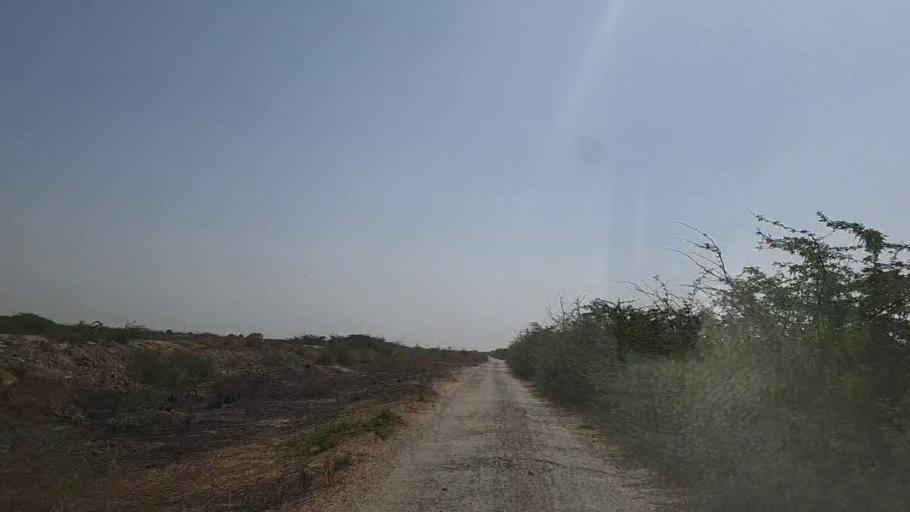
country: PK
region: Sindh
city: Naukot
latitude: 24.6286
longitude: 69.2711
